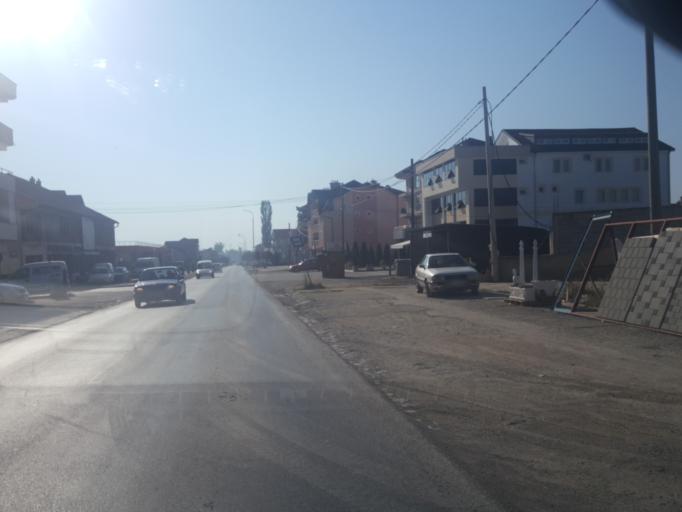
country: XK
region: Gjakova
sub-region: Komuna e Gjakoves
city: Gjakove
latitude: 42.4045
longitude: 20.4108
